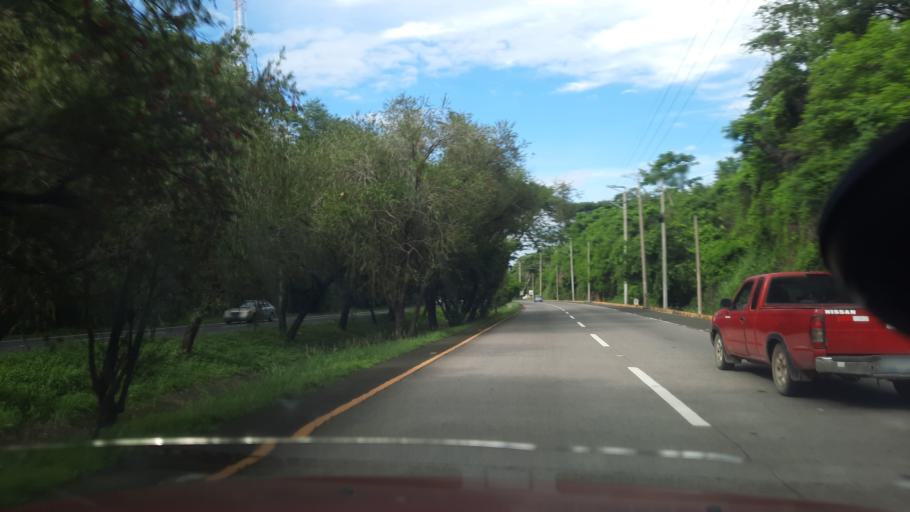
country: SV
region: La Paz
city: Olocuilta
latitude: 13.5352
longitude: -89.1121
